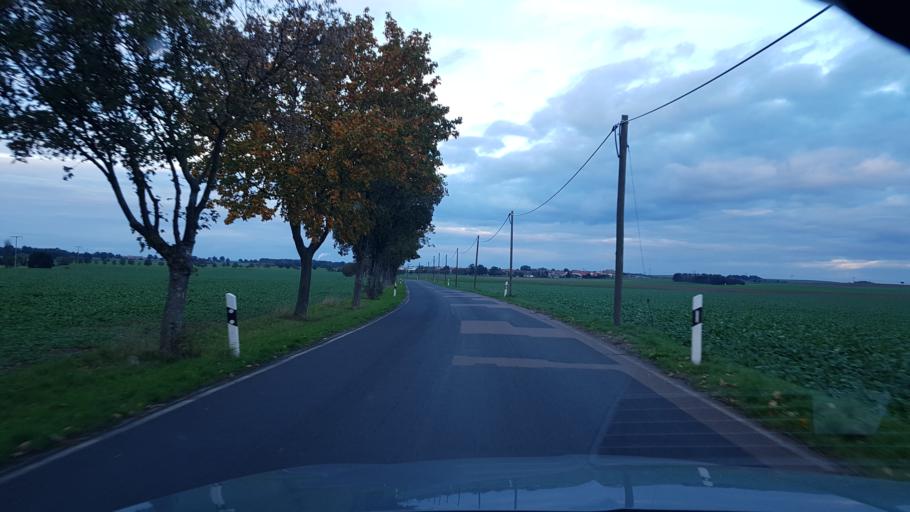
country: DE
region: Saxony
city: Priestewitz
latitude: 51.2427
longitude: 13.5653
